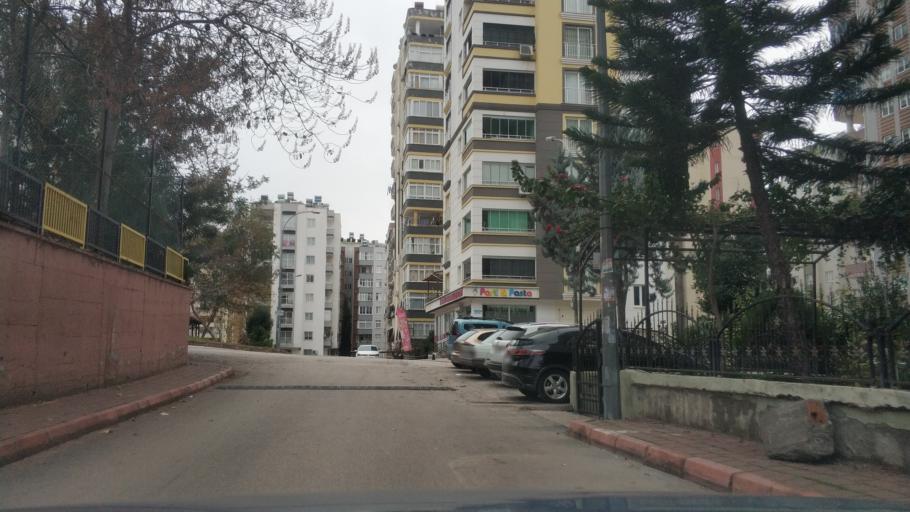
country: TR
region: Adana
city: Seyhan
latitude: 37.0543
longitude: 35.2795
